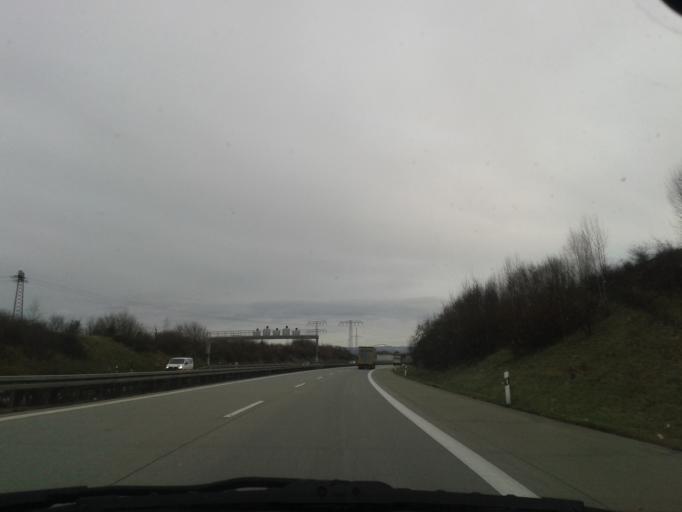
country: DE
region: Saxony
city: Freital
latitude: 51.0361
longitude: 13.6561
